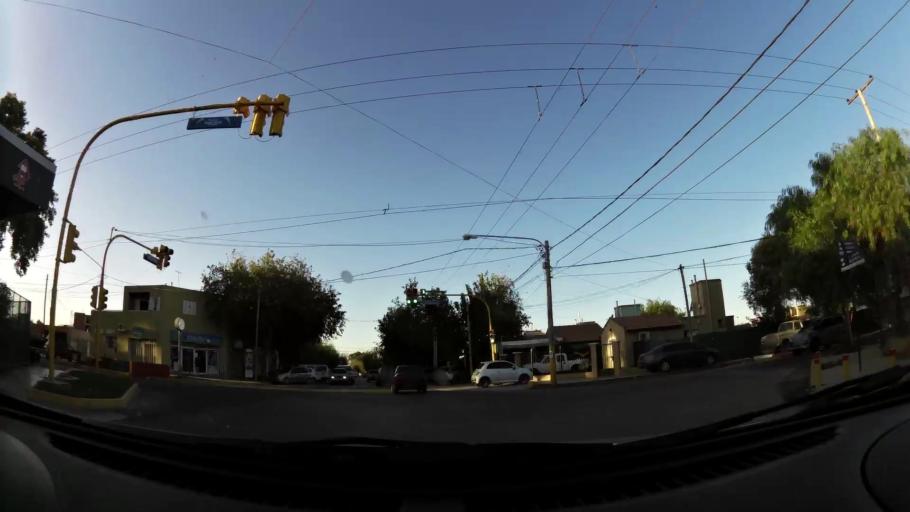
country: AR
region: San Juan
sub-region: Departamento de Santa Lucia
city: Santa Lucia
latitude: -31.5387
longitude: -68.4935
